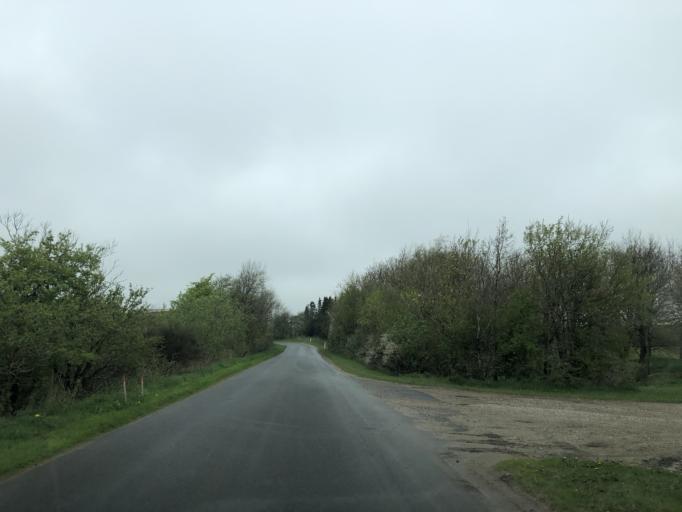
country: DK
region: Central Jutland
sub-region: Lemvig Kommune
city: Lemvig
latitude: 56.5127
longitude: 8.3129
